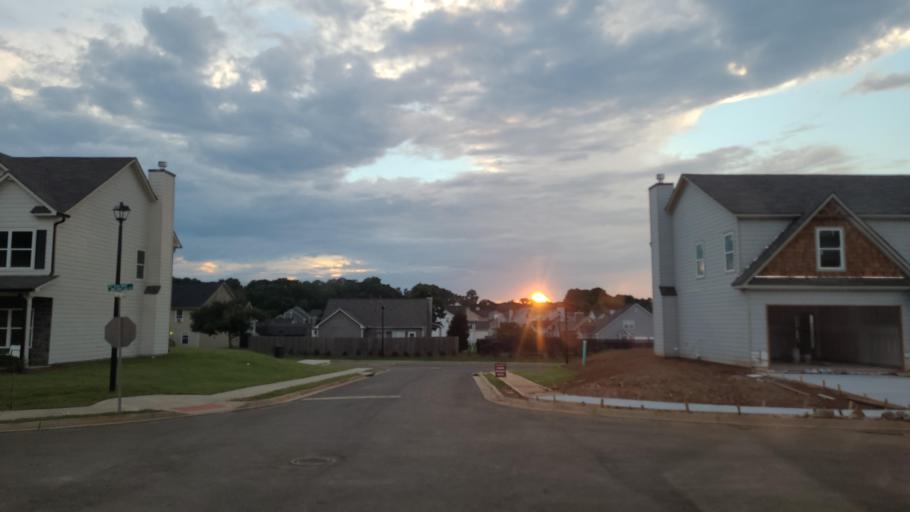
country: US
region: Georgia
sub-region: Bartow County
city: Cartersville
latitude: 34.2121
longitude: -84.7867
